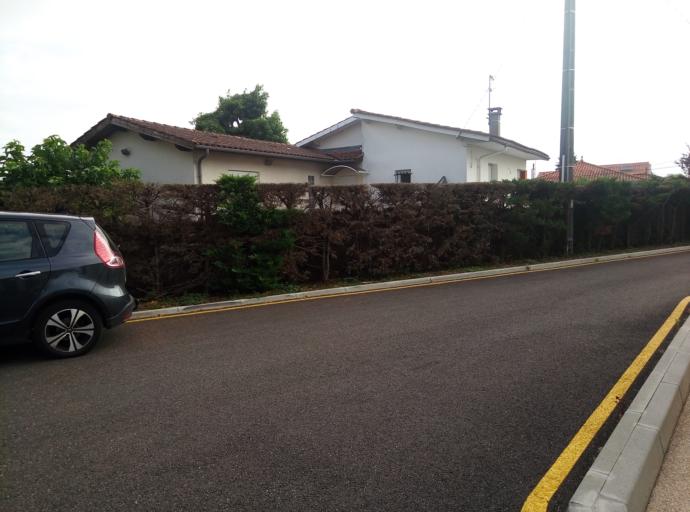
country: FR
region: Aquitaine
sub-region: Departement de la Gironde
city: Villenave-d'Ornon
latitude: 44.7831
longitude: -0.5714
